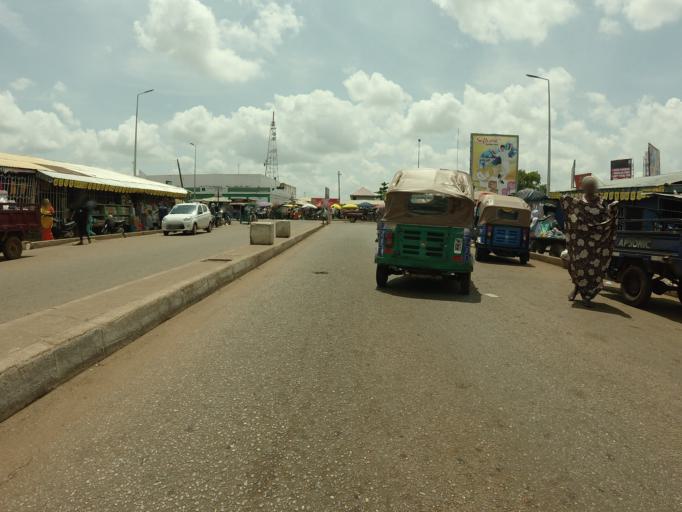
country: GH
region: Northern
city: Tamale
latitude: 9.4032
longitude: -0.8419
